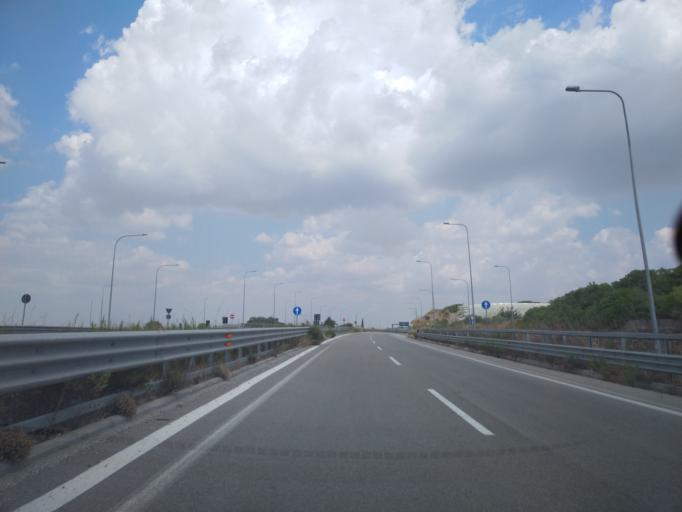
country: IT
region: Sicily
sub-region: Agrigento
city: Canicatti
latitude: 37.3826
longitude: 13.8114
